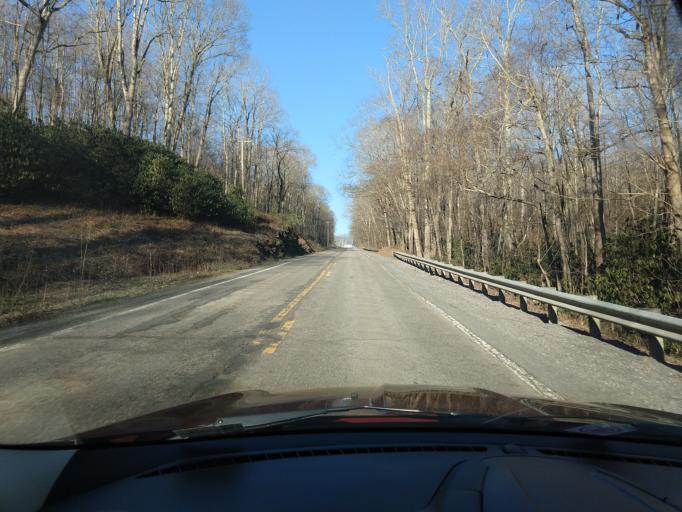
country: US
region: West Virginia
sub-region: Fayette County
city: Fayetteville
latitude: 38.0496
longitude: -80.9503
